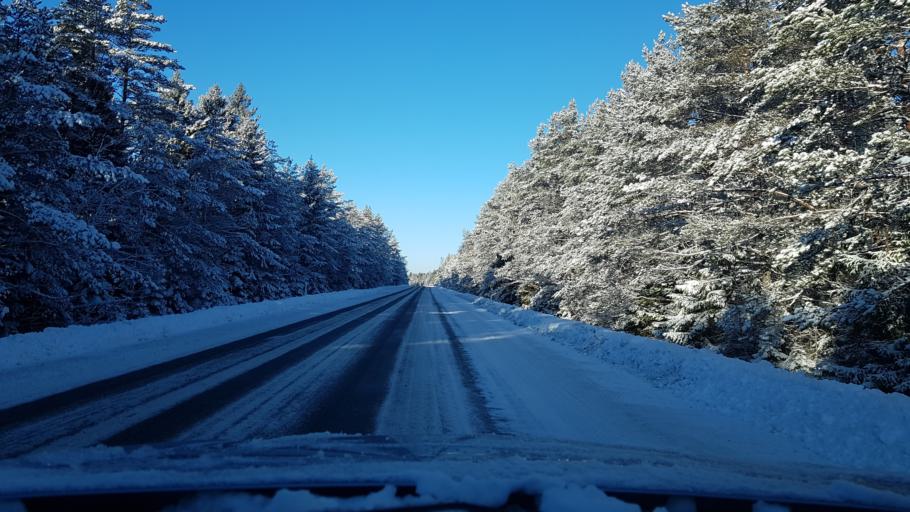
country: EE
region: Hiiumaa
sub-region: Kaerdla linn
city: Kardla
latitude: 58.9857
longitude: 22.7983
